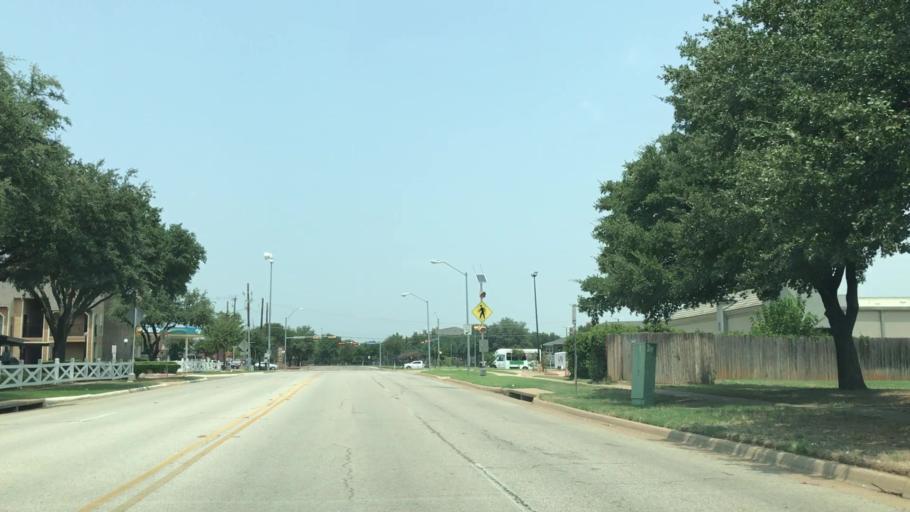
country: US
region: Texas
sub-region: Tarrant County
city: Euless
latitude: 32.8502
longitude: -97.0727
